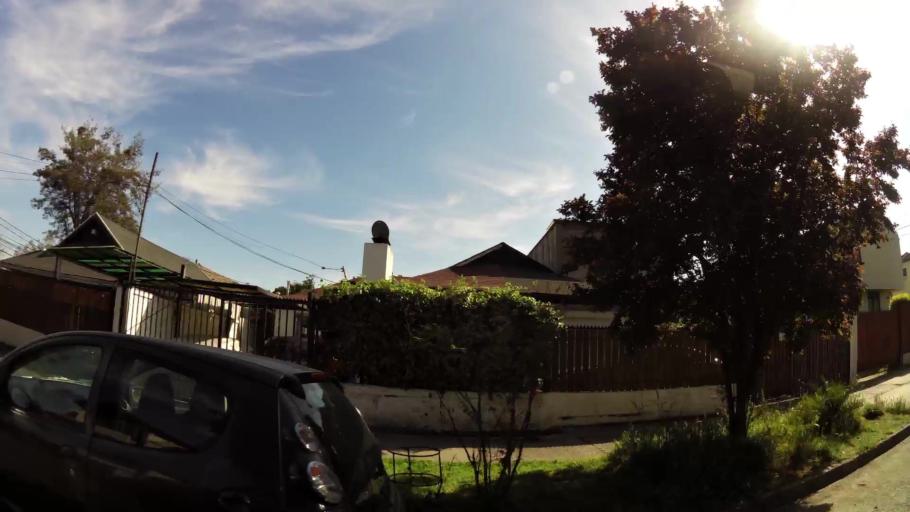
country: CL
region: Santiago Metropolitan
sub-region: Provincia de Santiago
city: Villa Presidente Frei, Nunoa, Santiago, Chile
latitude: -33.4527
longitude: -70.5550
